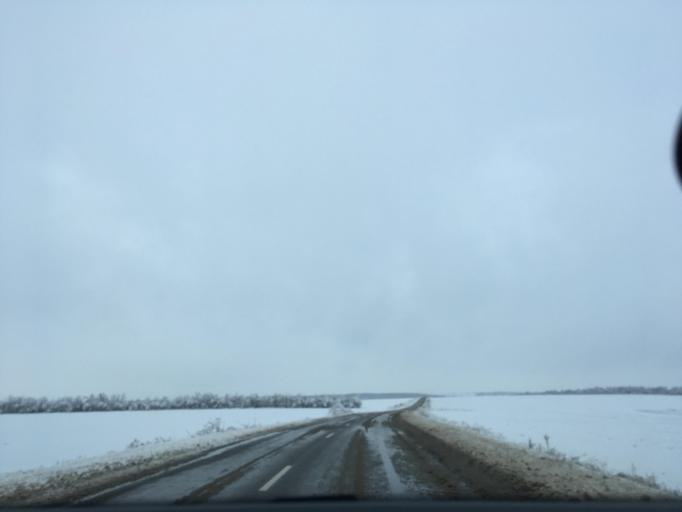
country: RU
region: Voronezj
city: Ol'khovatka
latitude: 50.1351
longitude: 39.1994
